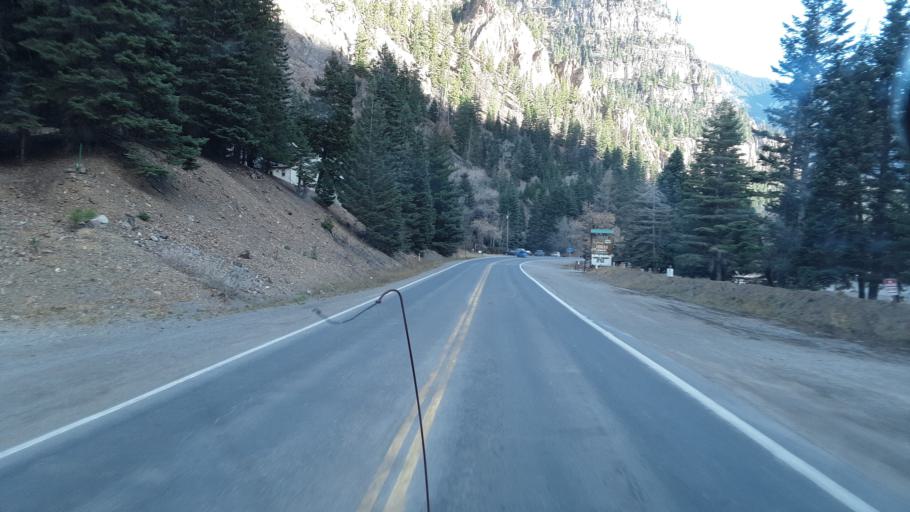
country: US
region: Colorado
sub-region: Ouray County
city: Ouray
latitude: 38.0356
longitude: -107.6770
